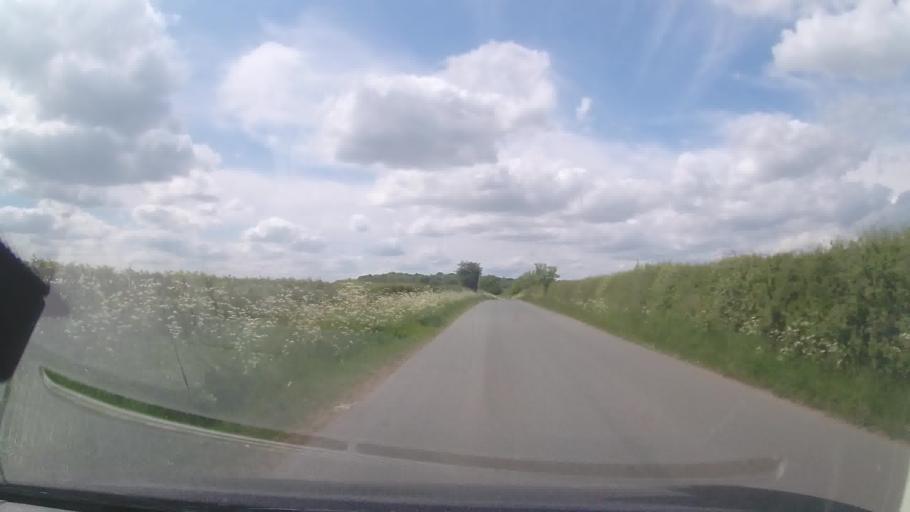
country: GB
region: England
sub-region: Shropshire
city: Shawbury
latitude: 52.8072
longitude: -2.6613
